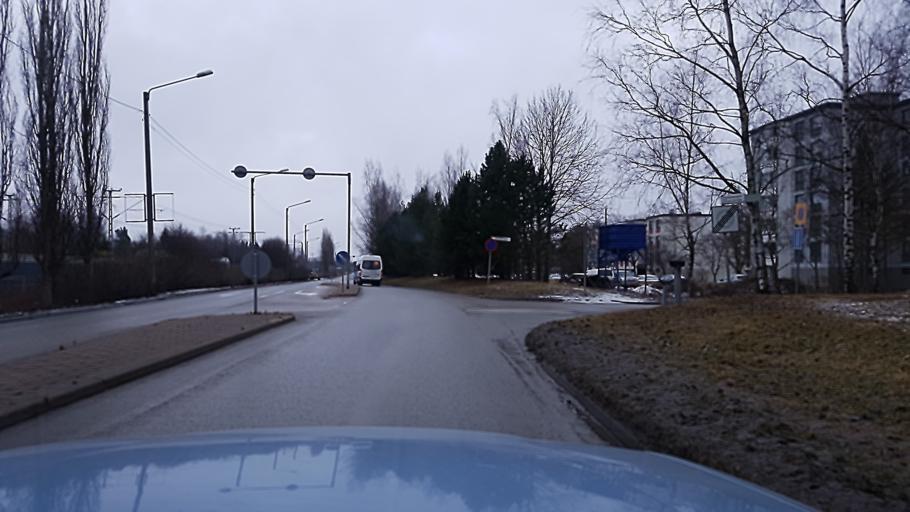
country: FI
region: Uusimaa
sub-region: Helsinki
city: Vantaa
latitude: 60.2734
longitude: 25.0348
